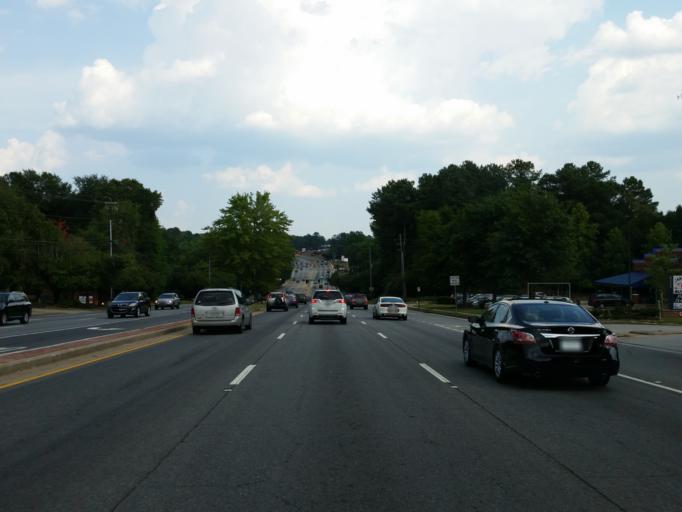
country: US
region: Georgia
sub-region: Fulton County
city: Roswell
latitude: 34.0272
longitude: -84.3341
